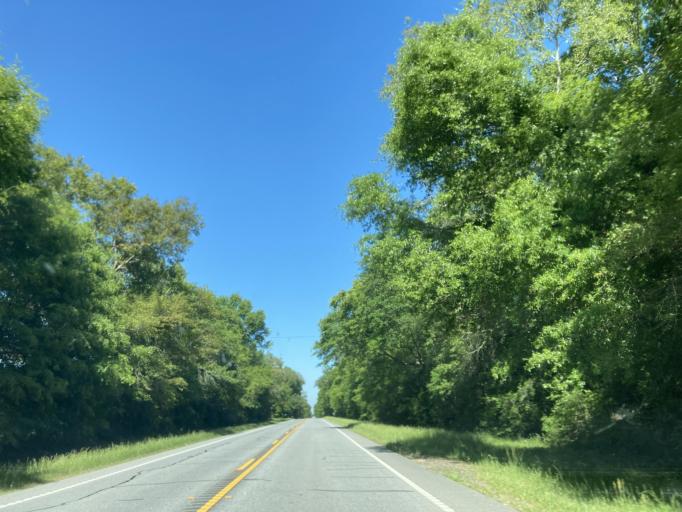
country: US
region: Georgia
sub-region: Baker County
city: Newton
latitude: 31.2542
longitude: -84.4200
